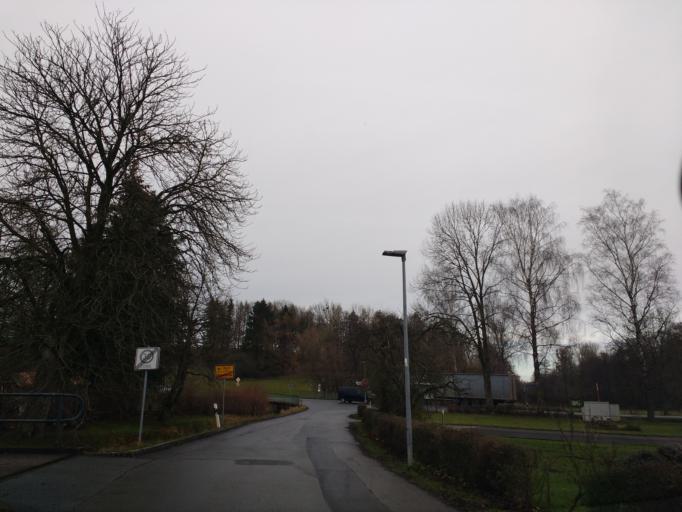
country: DE
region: North Rhine-Westphalia
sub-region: Regierungsbezirk Detmold
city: Horn
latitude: 51.8562
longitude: 8.9605
